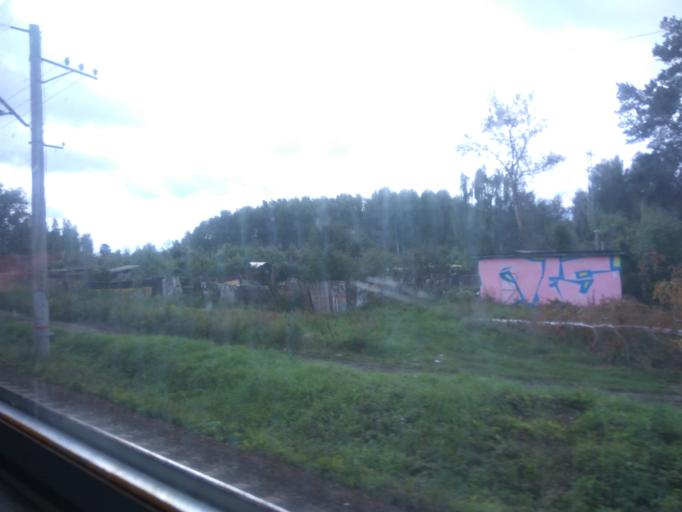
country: RU
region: Moskovskaya
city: Beloozerskiy
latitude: 55.4599
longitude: 38.4538
